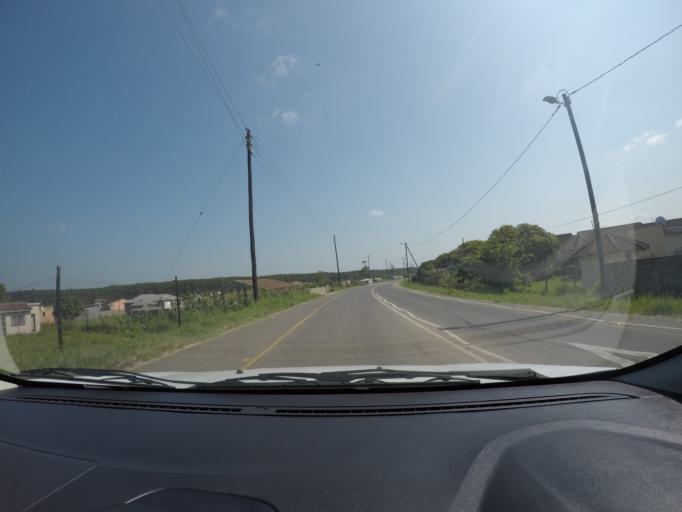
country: ZA
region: KwaZulu-Natal
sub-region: uThungulu District Municipality
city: eSikhawini
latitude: -28.8909
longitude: 31.8809
